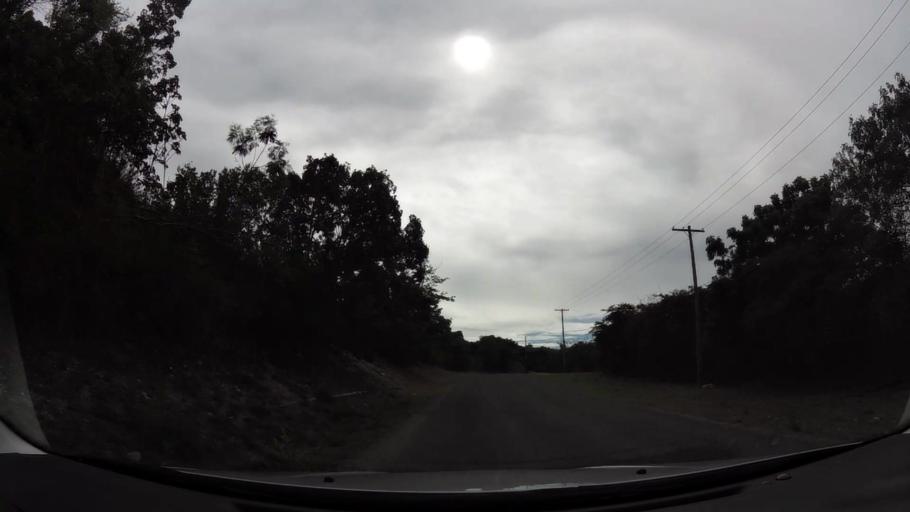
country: AG
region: Saint Peter
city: Parham
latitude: 17.0690
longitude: -61.7345
